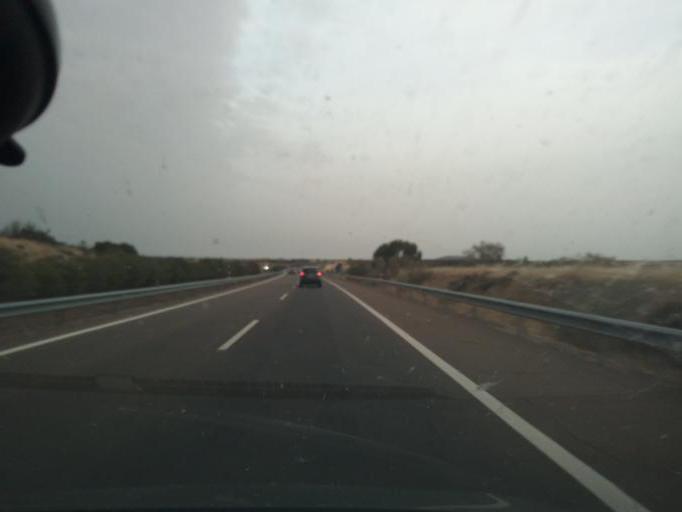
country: ES
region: Extremadura
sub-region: Provincia de Badajoz
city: Trujillanos
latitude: 38.9482
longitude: -6.2811
